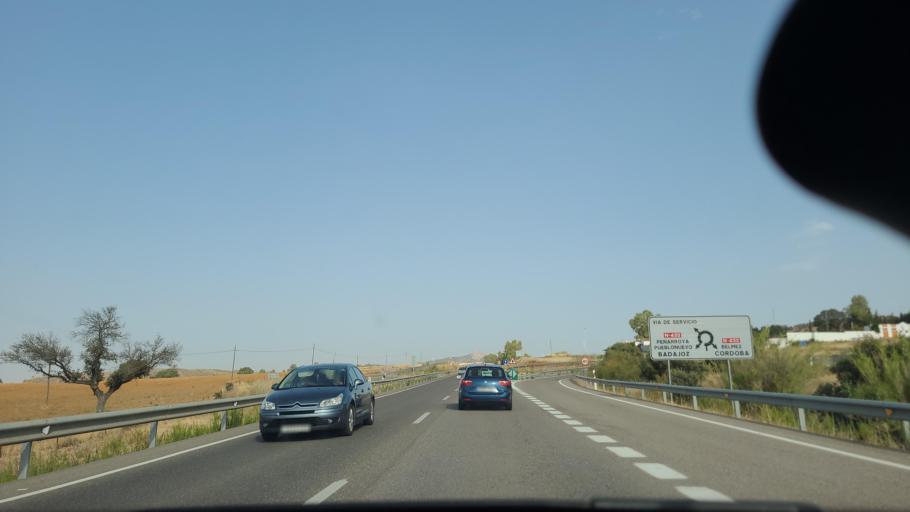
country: ES
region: Andalusia
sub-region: Province of Cordoba
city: Belmez
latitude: 38.2898
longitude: -5.2252
